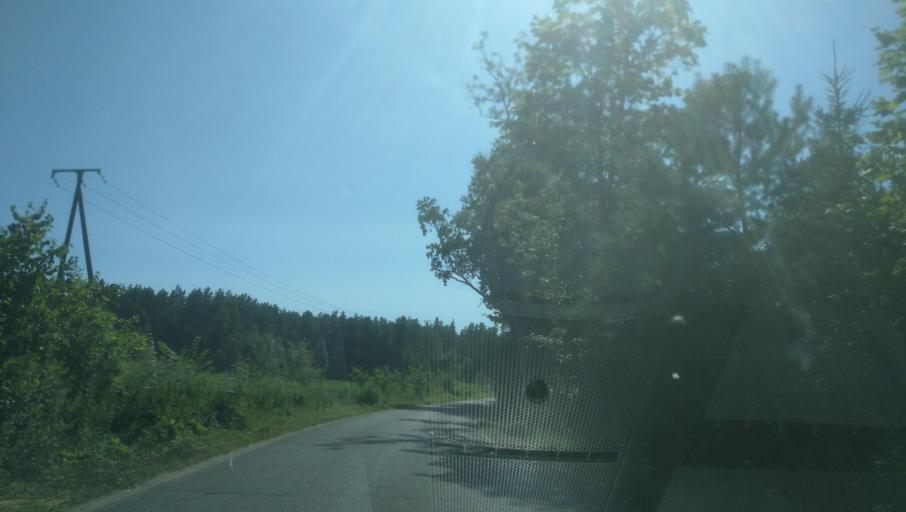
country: LV
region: Cesu Rajons
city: Cesis
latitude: 57.2904
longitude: 25.2317
